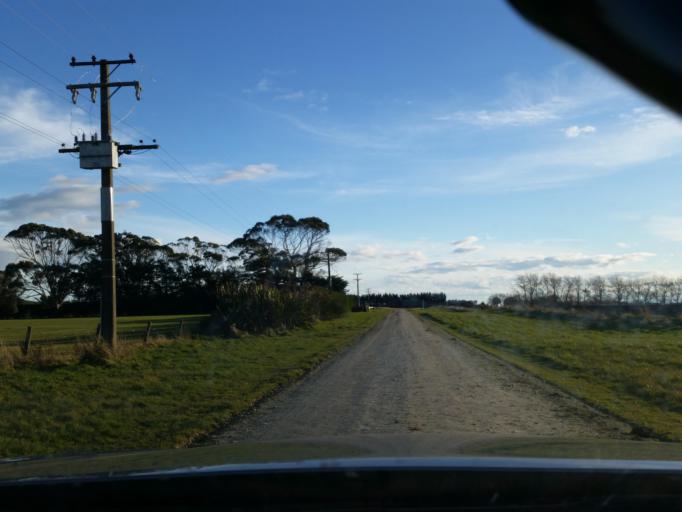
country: NZ
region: Southland
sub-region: Invercargill City
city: Invercargill
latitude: -46.3417
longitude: 168.6515
